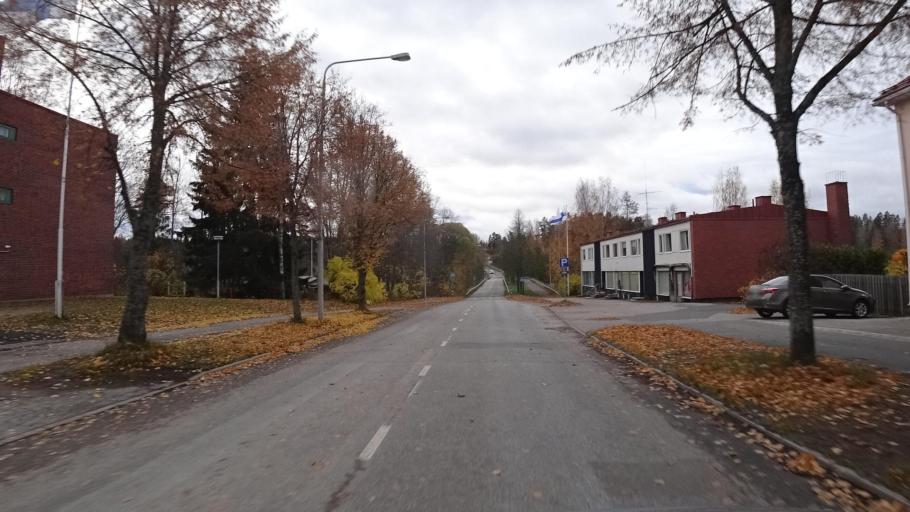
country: FI
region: Central Finland
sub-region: Joutsa
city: Joutsa
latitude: 61.7390
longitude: 26.1119
